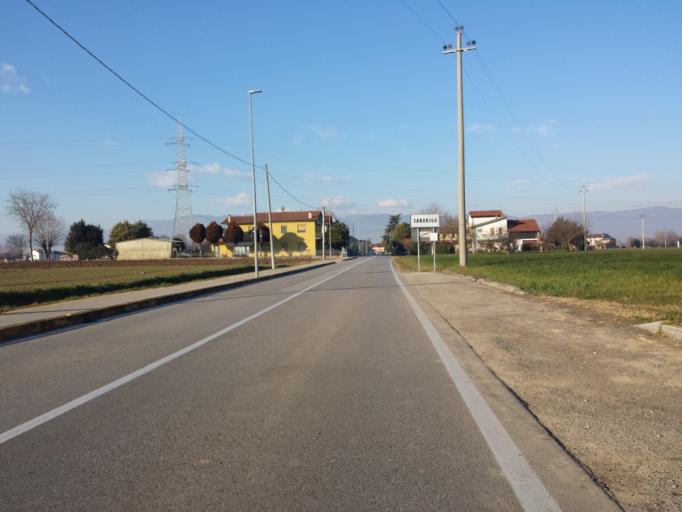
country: IT
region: Veneto
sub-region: Provincia di Vicenza
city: Sandrigo
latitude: 45.6481
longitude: 11.6058
